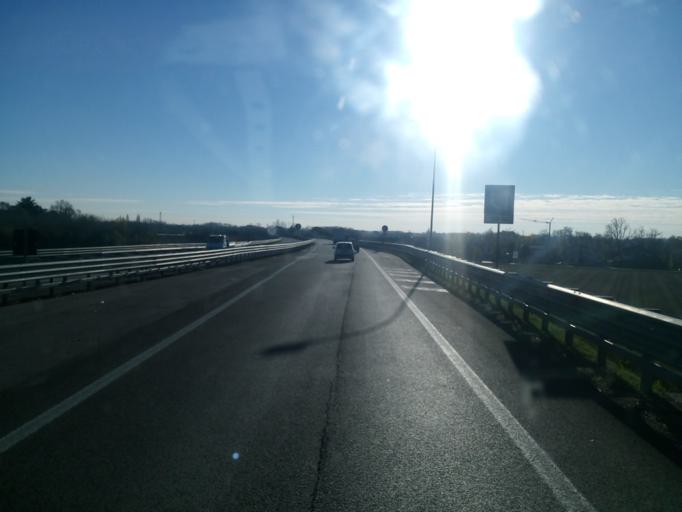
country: IT
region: Veneto
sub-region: Provincia di Treviso
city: Sant'Andrea
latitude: 45.6684
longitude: 11.9044
